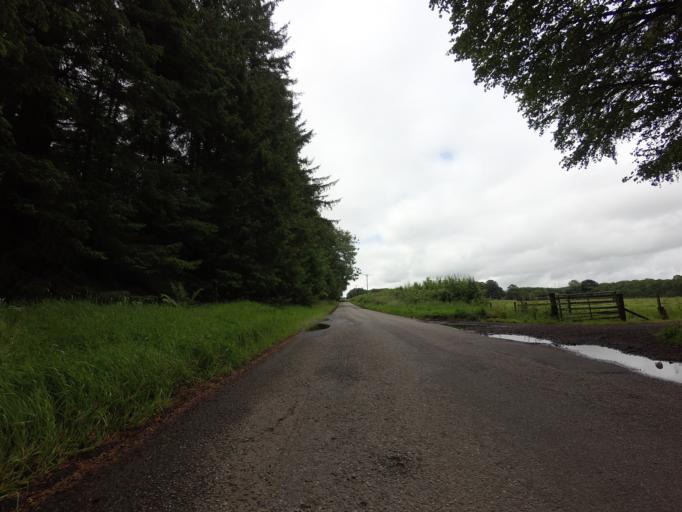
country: GB
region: Scotland
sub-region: Aberdeenshire
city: Mintlaw
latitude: 57.5311
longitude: -2.1524
